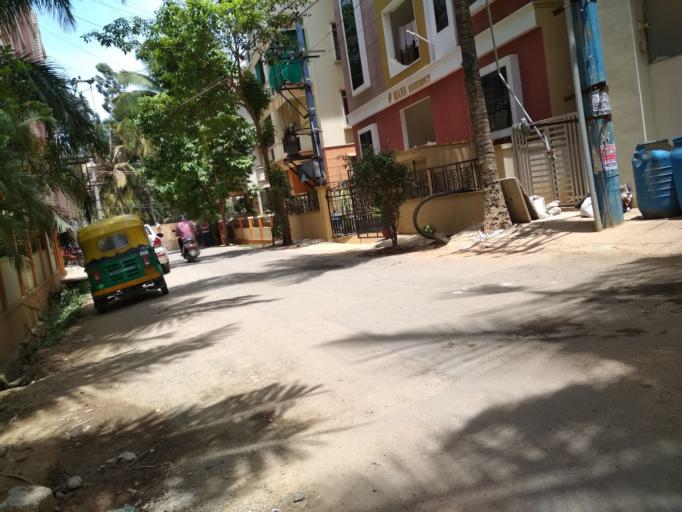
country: IN
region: Karnataka
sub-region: Bangalore Urban
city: Bangalore
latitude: 12.9236
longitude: 77.6741
